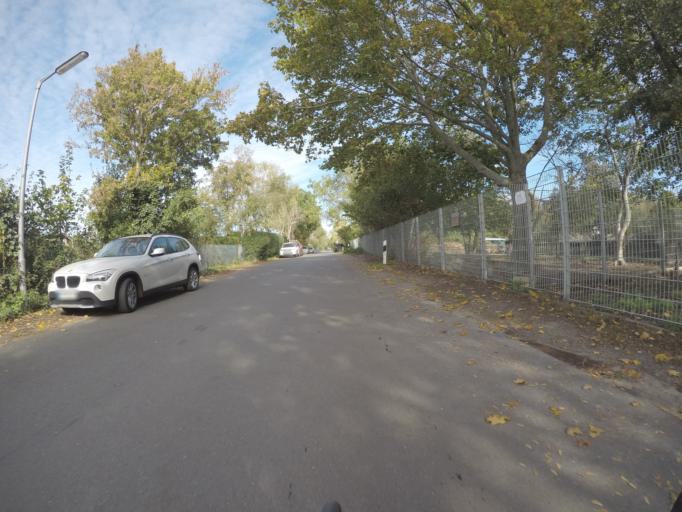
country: DE
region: Berlin
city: Marienfelde
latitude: 52.4011
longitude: 13.3615
